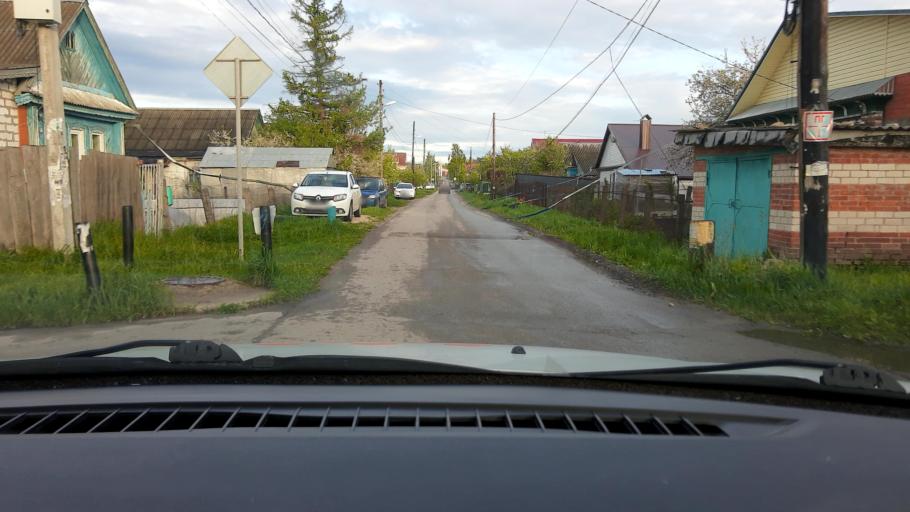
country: RU
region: Nizjnij Novgorod
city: Kstovo
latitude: 56.1729
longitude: 44.1706
